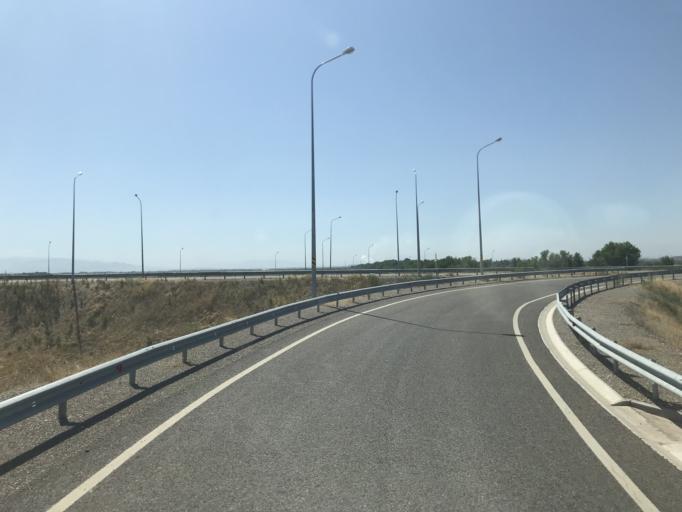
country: KZ
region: Zhambyl
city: Taraz
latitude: 42.9957
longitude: 71.2363
